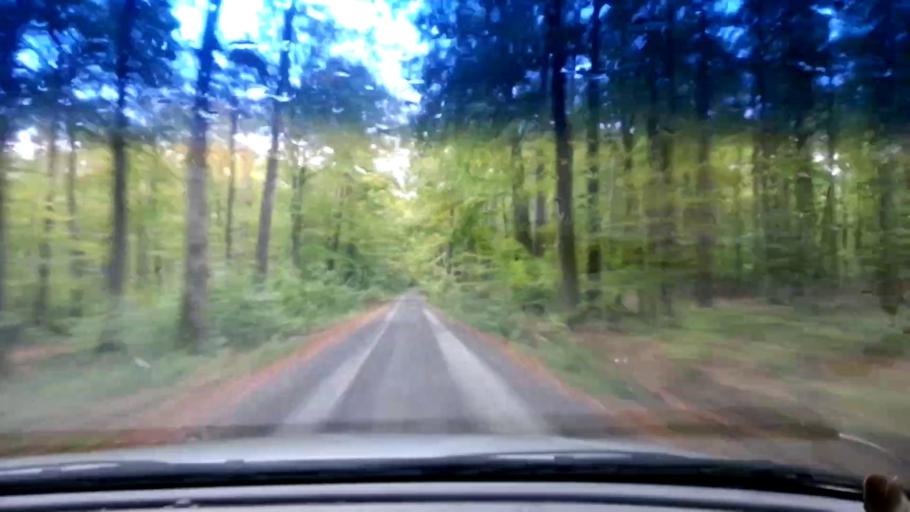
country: DE
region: Bavaria
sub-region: Upper Franconia
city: Burgwindheim
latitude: 49.8501
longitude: 10.6397
